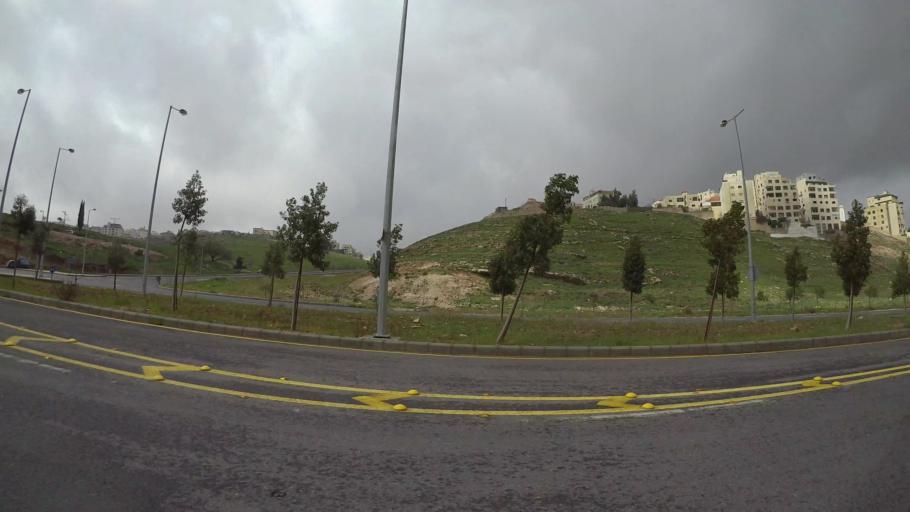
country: JO
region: Amman
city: Al Bunayyat ash Shamaliyah
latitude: 31.9366
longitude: 35.8993
